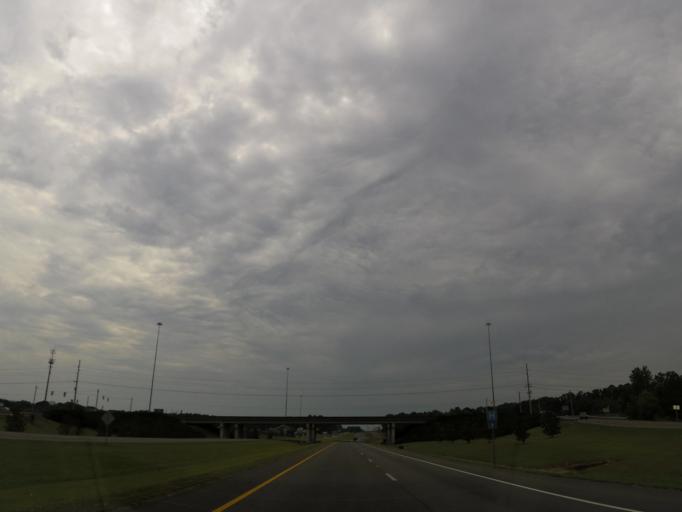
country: US
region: Alabama
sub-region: Jackson County
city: Scottsboro
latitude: 34.6651
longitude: -86.0137
